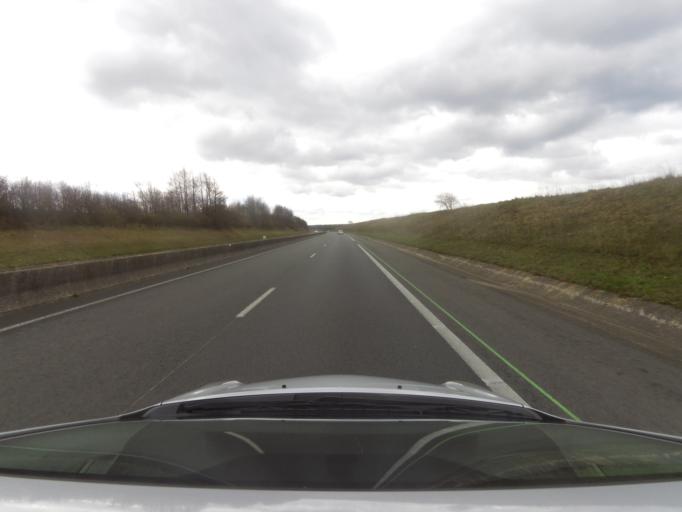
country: FR
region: Nord-Pas-de-Calais
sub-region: Departement du Pas-de-Calais
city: Saint-Josse
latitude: 50.4560
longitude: 1.6979
